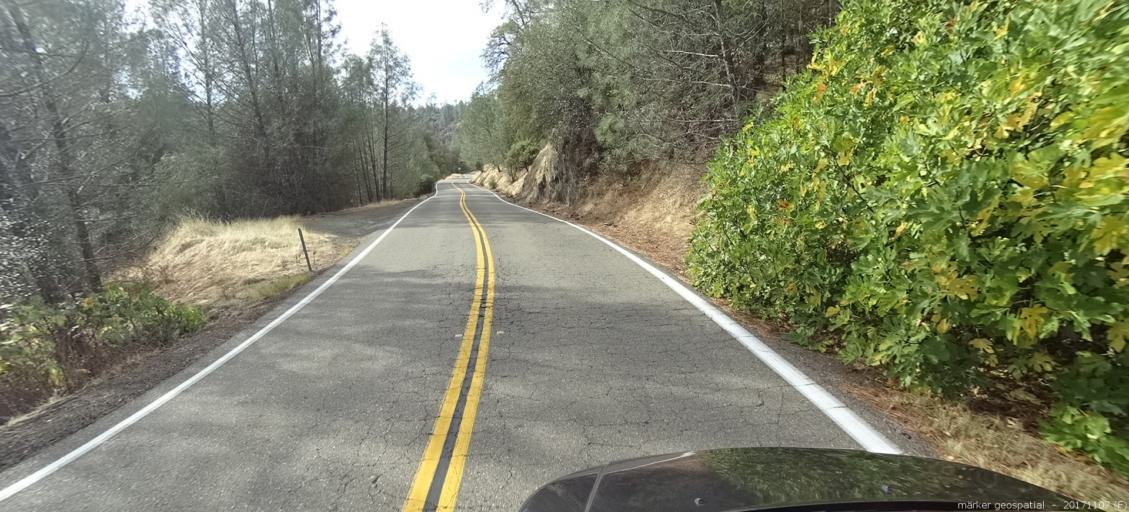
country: US
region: California
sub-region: Shasta County
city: Shasta
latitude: 40.5143
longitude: -122.5186
